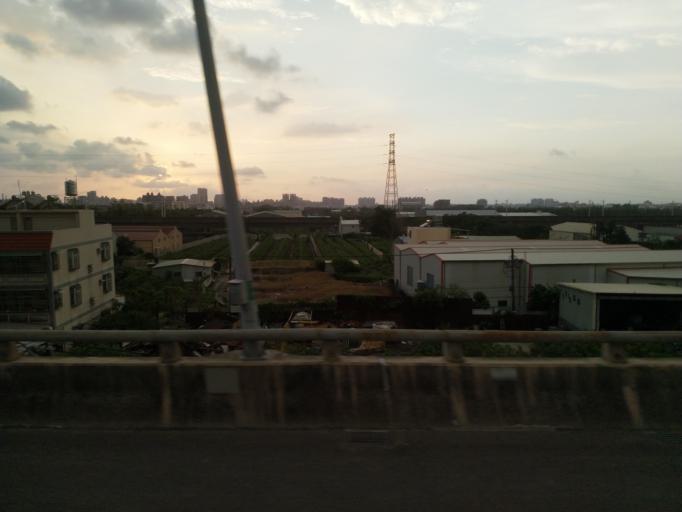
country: TW
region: Taiwan
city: Fengshan
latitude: 22.7361
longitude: 120.3611
